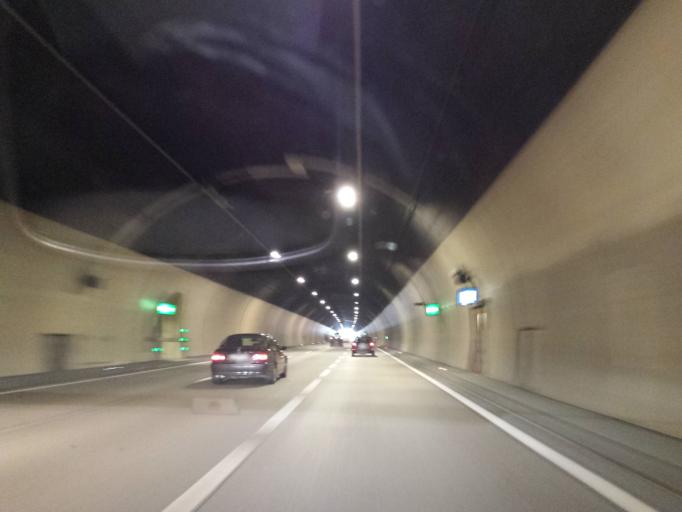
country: AT
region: Styria
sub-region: Politischer Bezirk Graz-Umgebung
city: Gratkorn
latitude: 47.1230
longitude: 15.3684
